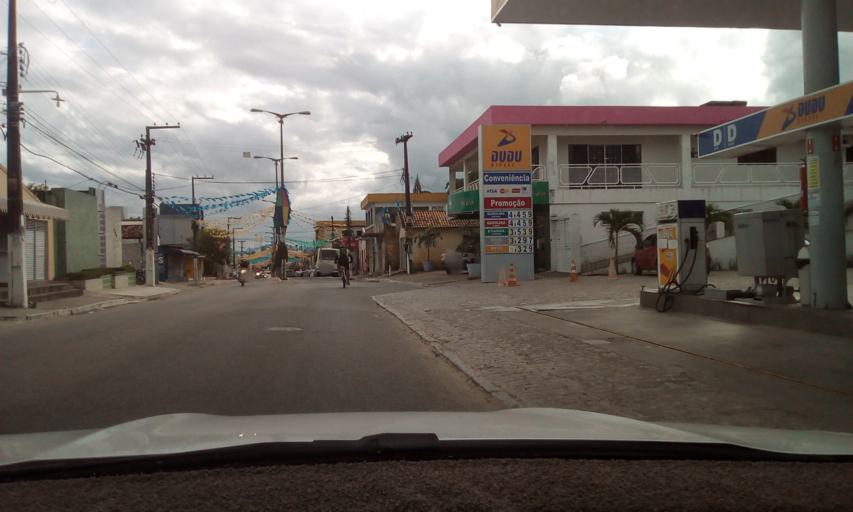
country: BR
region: Paraiba
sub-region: Mamanguape
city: Mamanguape
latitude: -6.8383
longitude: -35.1330
